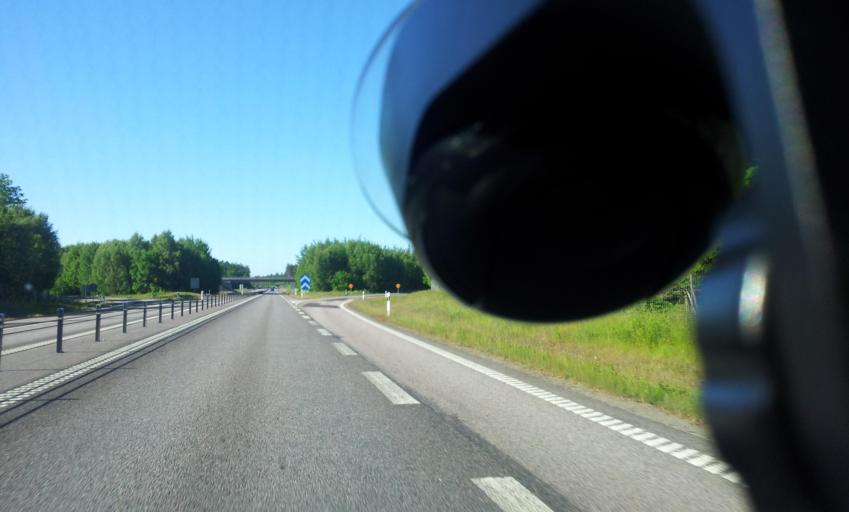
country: SE
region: Kalmar
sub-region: Kalmar Kommun
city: Ljungbyholm
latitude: 56.5551
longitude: 16.0864
